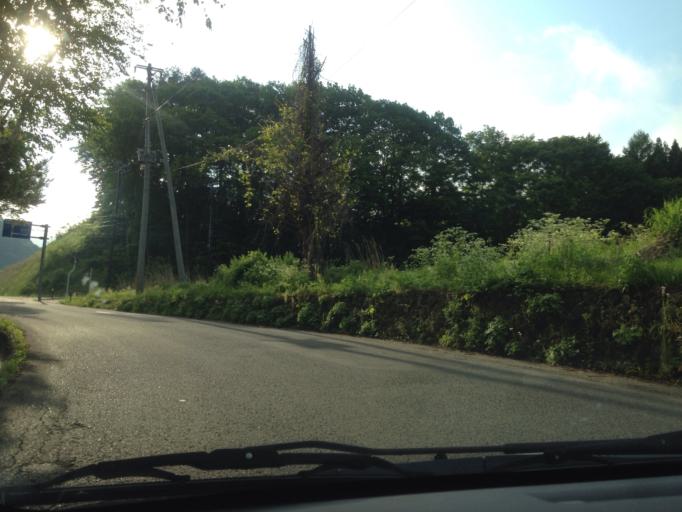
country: JP
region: Fukushima
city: Inawashiro
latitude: 37.3091
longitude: 139.8979
